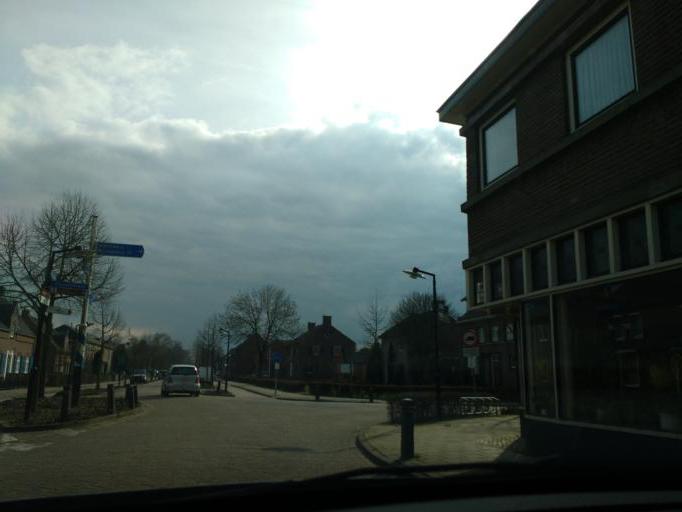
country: NL
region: North Brabant
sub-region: Gemeente Boxmeer
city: Overloon
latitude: 51.5972
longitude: 6.0124
